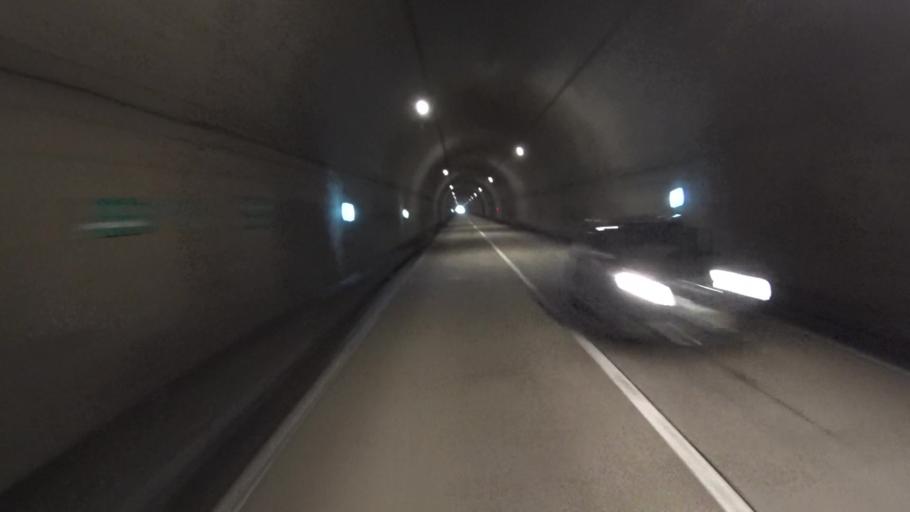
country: JP
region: Fukui
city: Obama
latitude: 35.3733
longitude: 135.5978
